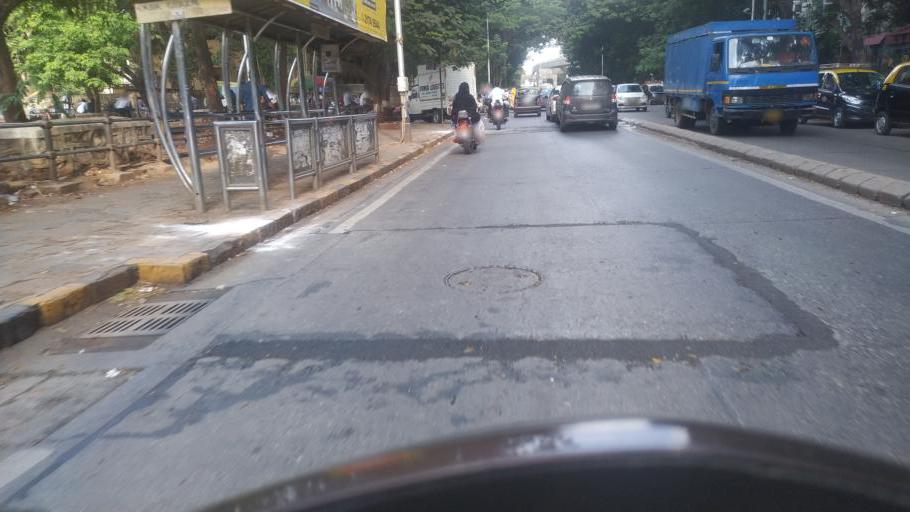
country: IN
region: Maharashtra
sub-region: Mumbai Suburban
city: Mumbai
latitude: 19.0198
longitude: 72.8545
